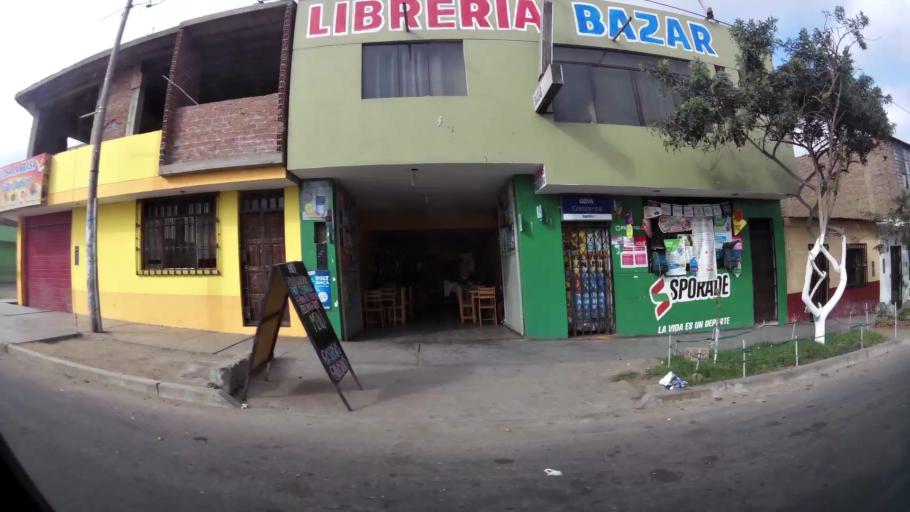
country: PE
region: La Libertad
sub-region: Provincia de Trujillo
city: La Esperanza
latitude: -8.0744
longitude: -79.0478
